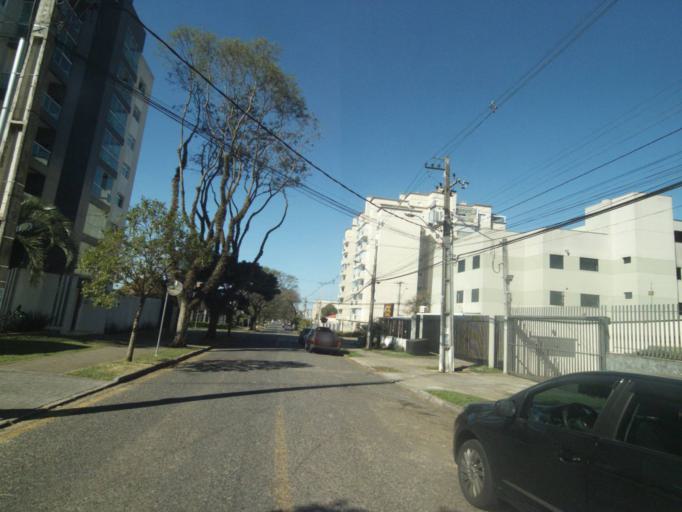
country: BR
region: Parana
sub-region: Curitiba
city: Curitiba
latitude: -25.3986
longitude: -49.2398
